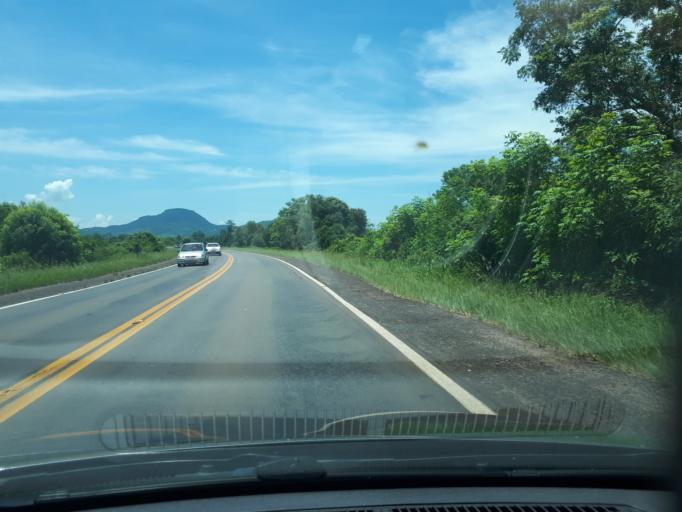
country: BR
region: Rio Grande do Sul
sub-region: Candelaria
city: Candelaria
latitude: -29.7247
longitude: -52.9234
